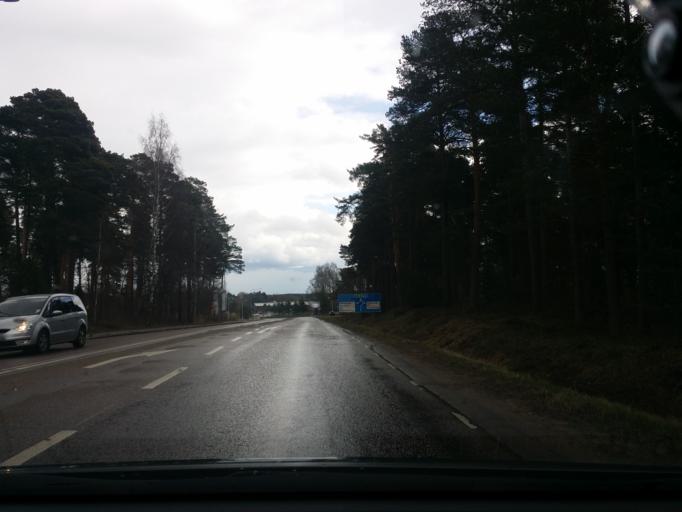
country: SE
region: Uppsala
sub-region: Enkopings Kommun
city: Enkoping
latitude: 59.6455
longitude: 17.1126
